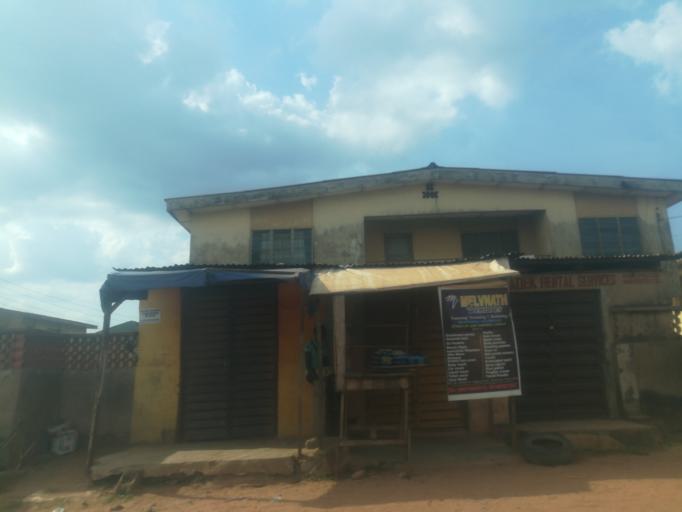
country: NG
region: Ogun
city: Abeokuta
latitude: 7.1145
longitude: 3.3147
